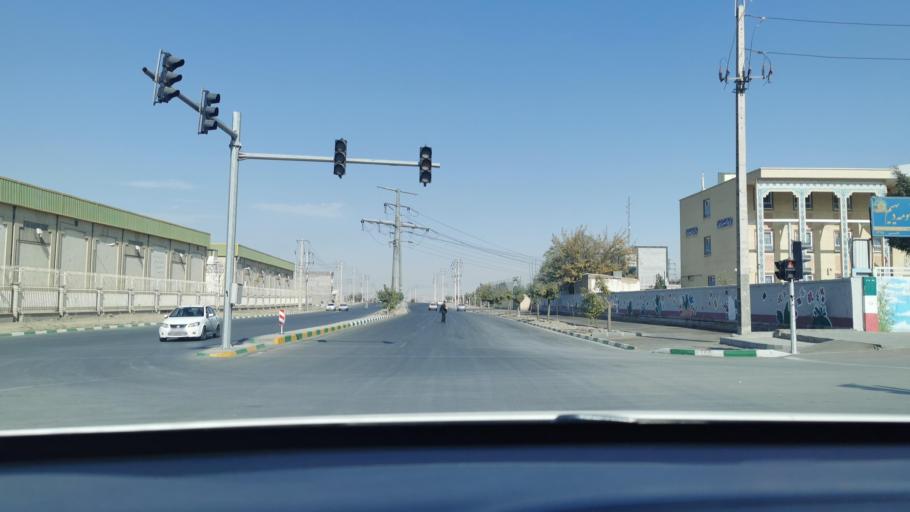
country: IR
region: Razavi Khorasan
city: Mashhad
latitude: 36.3410
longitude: 59.6086
